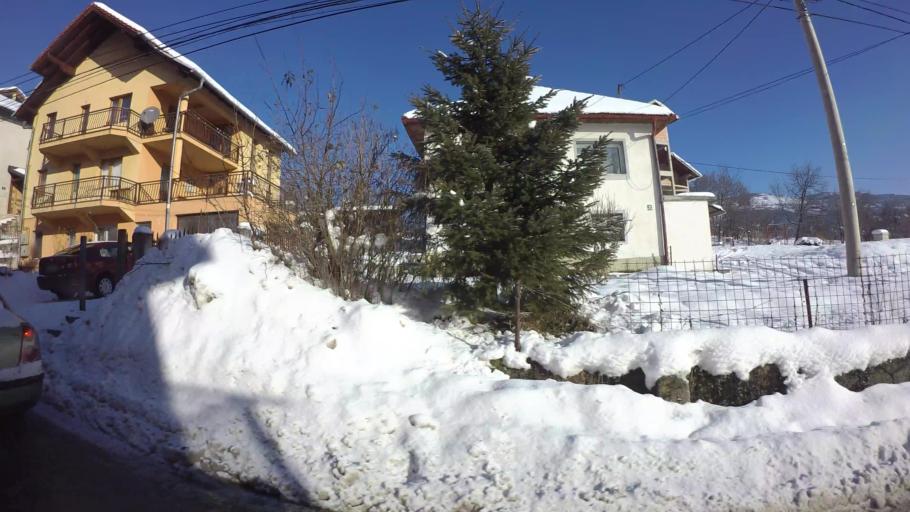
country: BA
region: Federation of Bosnia and Herzegovina
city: Kobilja Glava
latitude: 43.8814
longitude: 18.3921
